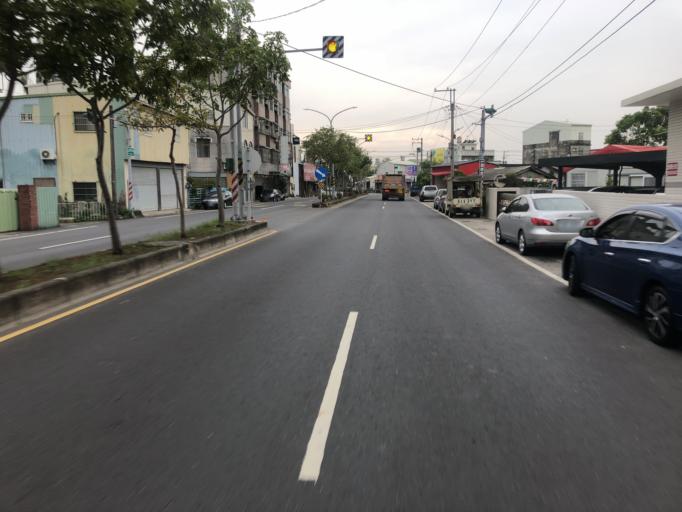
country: TW
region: Taiwan
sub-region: Tainan
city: Tainan
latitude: 23.1345
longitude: 120.2851
